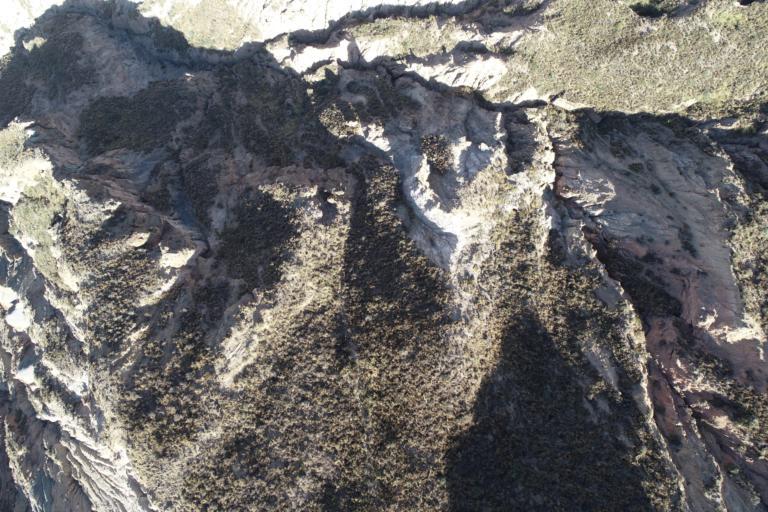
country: BO
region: La Paz
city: La Paz
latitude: -16.5524
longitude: -68.1049
